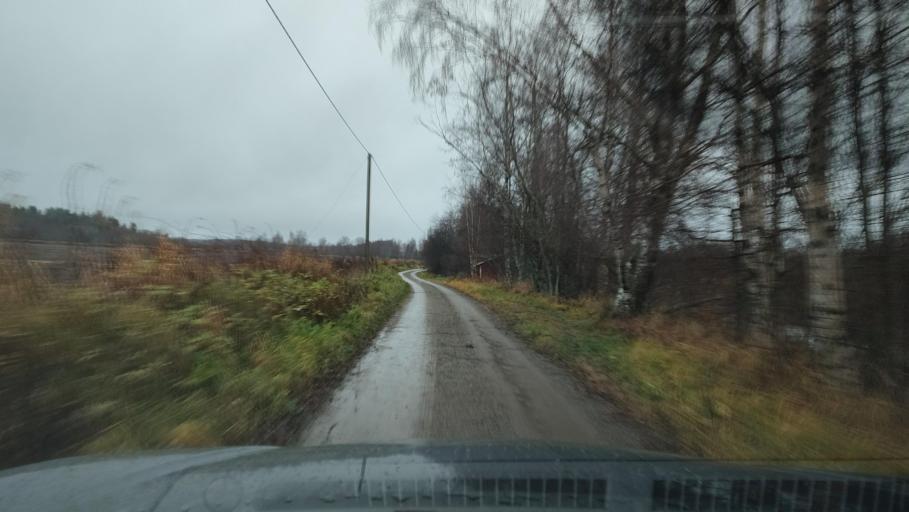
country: FI
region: Ostrobothnia
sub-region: Sydosterbotten
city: Kristinestad
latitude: 62.2303
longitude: 21.4496
